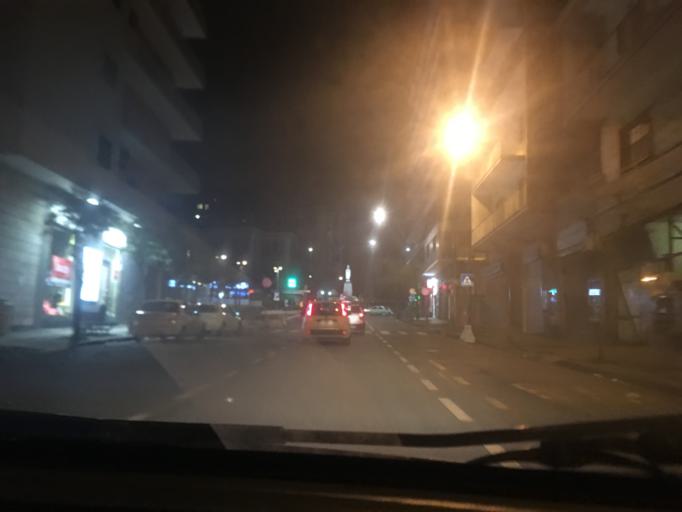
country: IT
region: Campania
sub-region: Provincia di Napoli
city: Napoli
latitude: 40.8527
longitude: 14.2305
